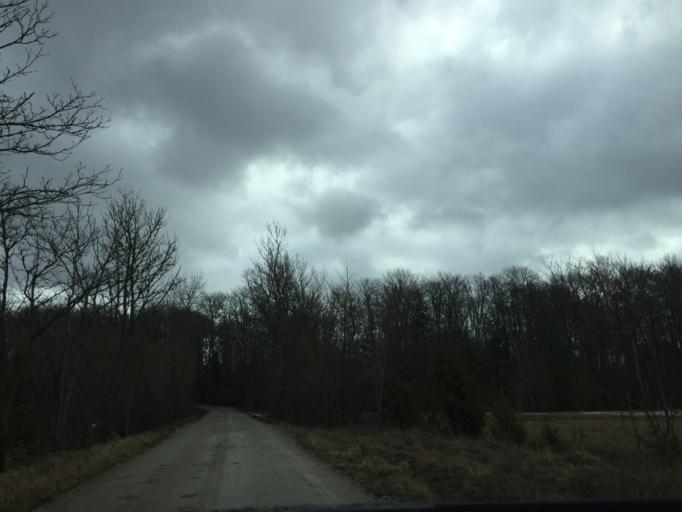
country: EE
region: Laeaene
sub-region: Haapsalu linn
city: Haapsalu
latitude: 58.6827
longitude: 23.5232
